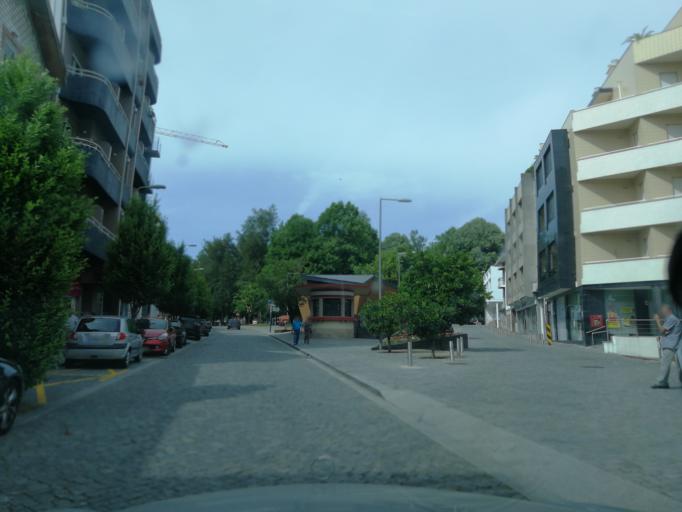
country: PT
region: Braga
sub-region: Vila Nova de Famalicao
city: Vila Nova de Famalicao
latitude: 41.4037
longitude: -8.5193
